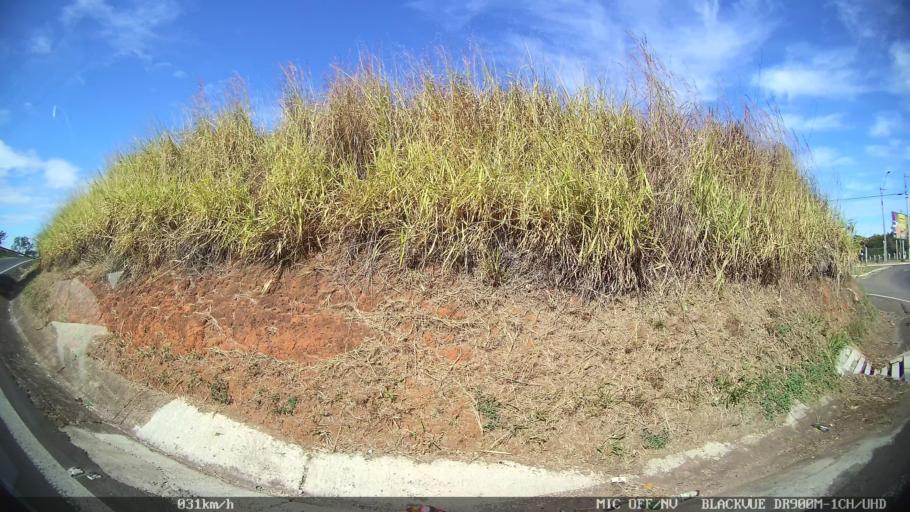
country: BR
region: Sao Paulo
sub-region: Sao Jose Do Rio Preto
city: Sao Jose do Rio Preto
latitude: -20.8134
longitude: -49.4811
